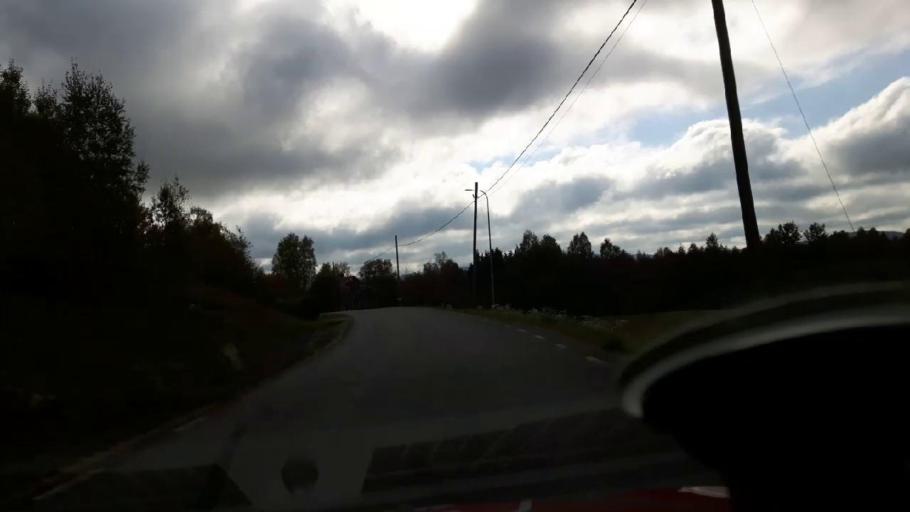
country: SE
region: Gaevleborg
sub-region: Ljusdals Kommun
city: Farila
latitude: 61.7887
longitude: 15.9194
